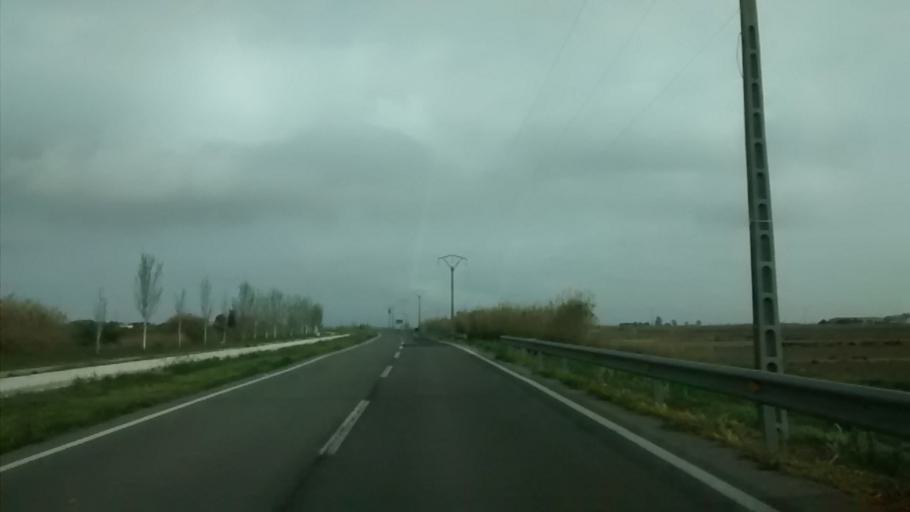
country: ES
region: Catalonia
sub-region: Provincia de Tarragona
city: Sant Carles de la Rapita
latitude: 40.6347
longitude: 0.6017
